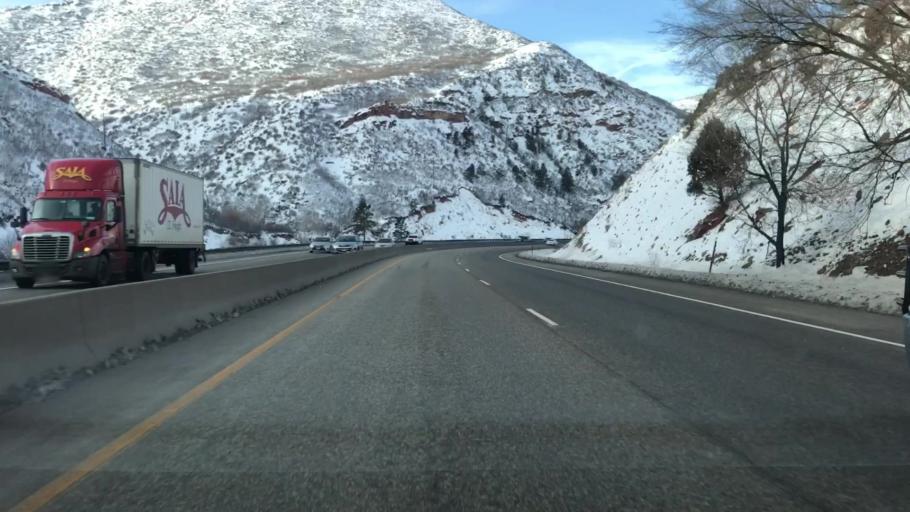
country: US
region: Colorado
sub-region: Garfield County
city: Glenwood Springs
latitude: 39.5577
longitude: -107.3959
